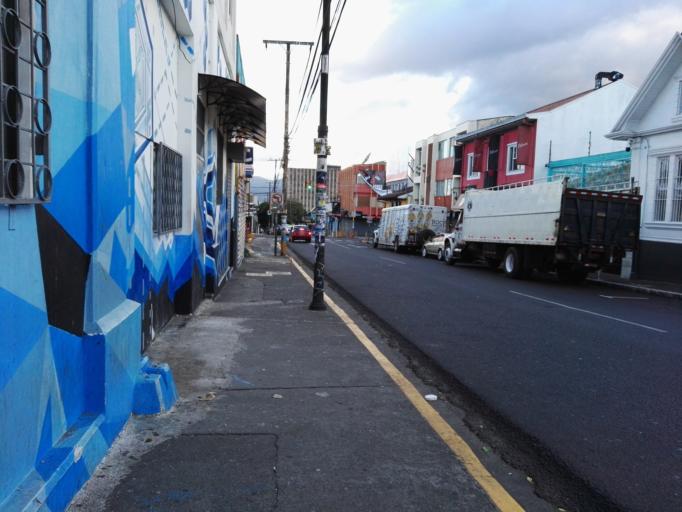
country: CR
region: San Jose
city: San Jose
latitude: 9.9338
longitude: -84.0691
